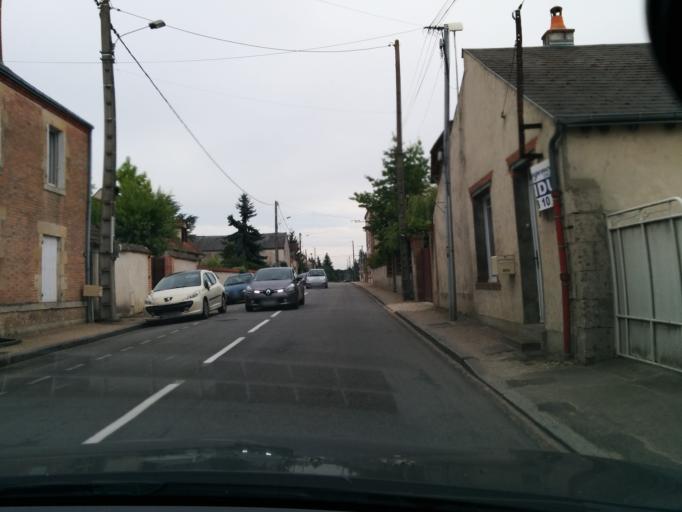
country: FR
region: Centre
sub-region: Departement du Loiret
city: Tigy
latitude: 47.7949
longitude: 2.1981
